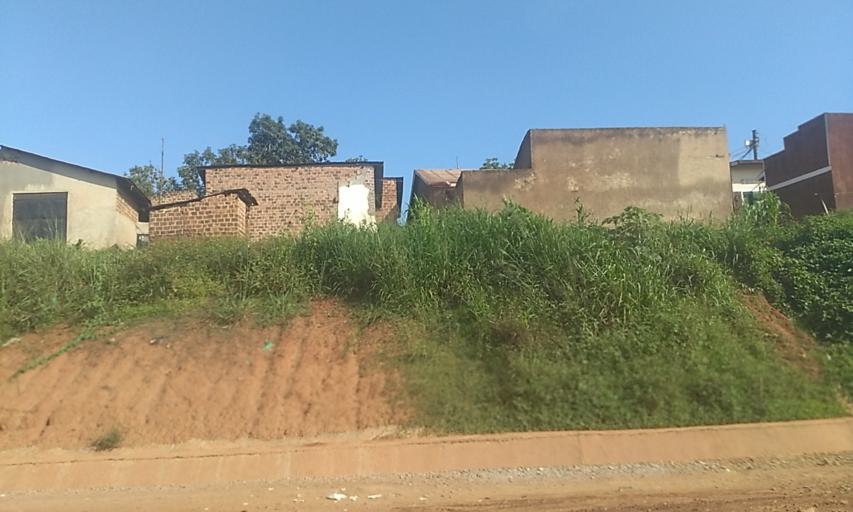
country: UG
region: Central Region
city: Kampala Central Division
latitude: 0.3293
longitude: 32.5255
